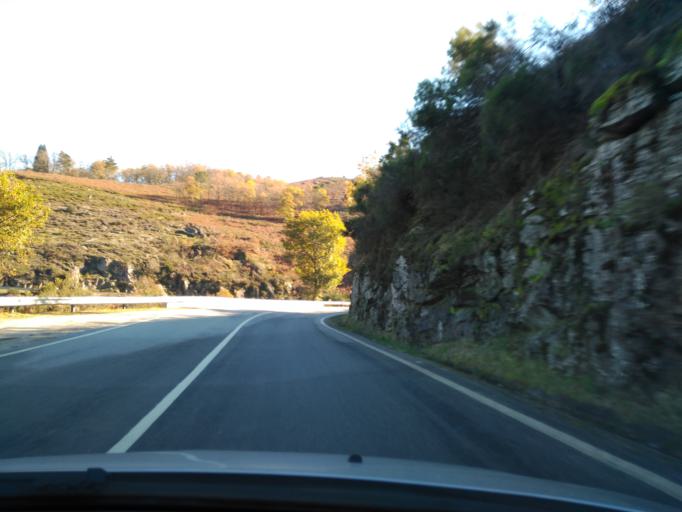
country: PT
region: Braga
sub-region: Vieira do Minho
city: Vieira do Minho
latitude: 41.6800
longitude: -8.0029
